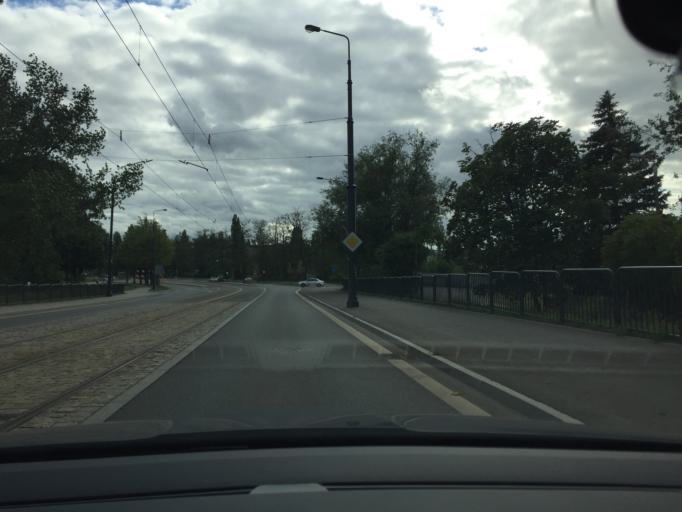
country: PL
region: Pomeranian Voivodeship
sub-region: Gdansk
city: Gdansk
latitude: 54.3538
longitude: 18.6744
